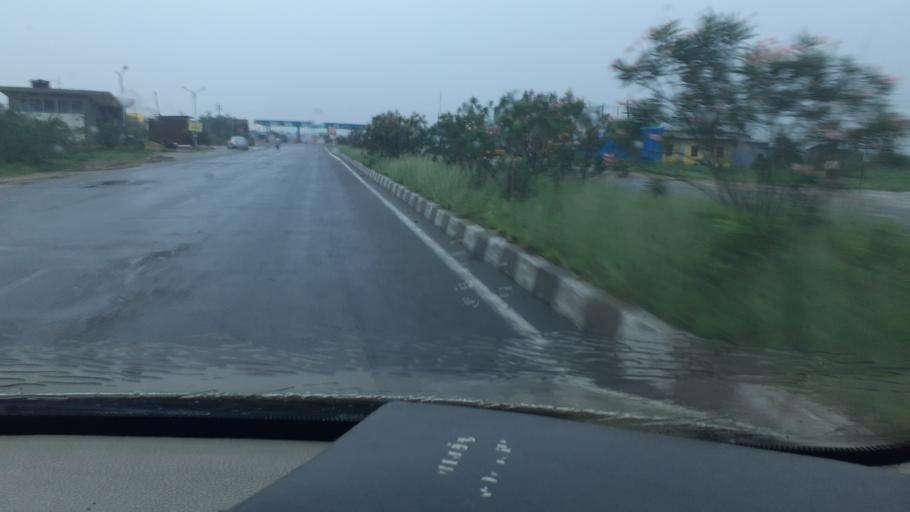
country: IN
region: Tamil Nadu
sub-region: Virudhunagar
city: Sattur
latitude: 9.3880
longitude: 77.9148
